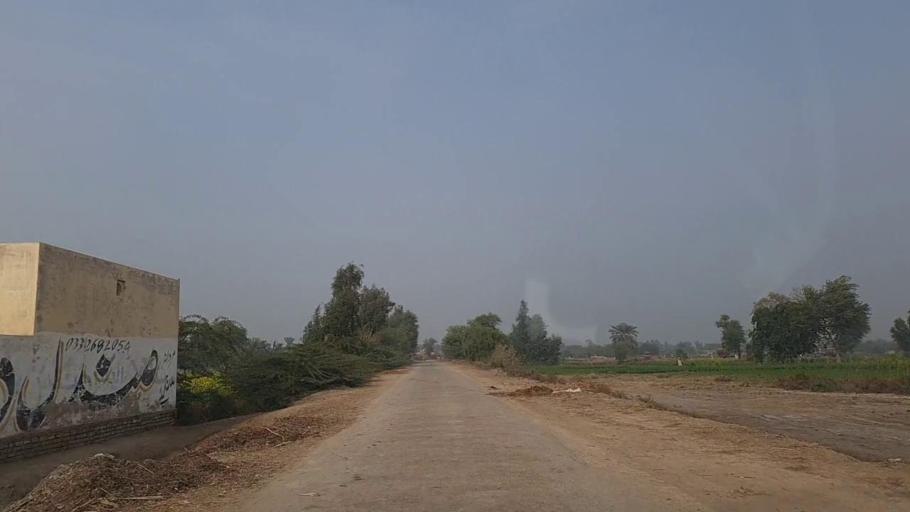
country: PK
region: Sindh
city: Sanghar
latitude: 26.0835
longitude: 68.8964
